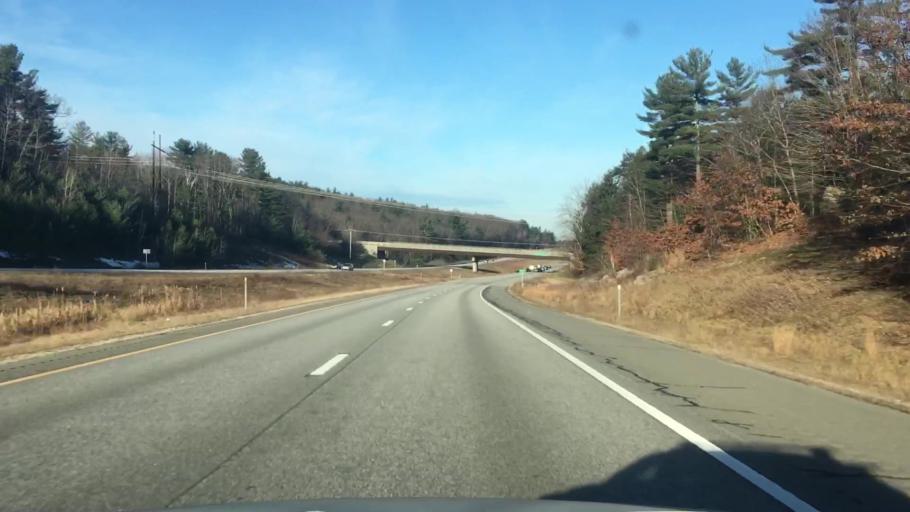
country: US
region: New Hampshire
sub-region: Rockingham County
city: Candia
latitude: 43.0326
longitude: -71.2519
